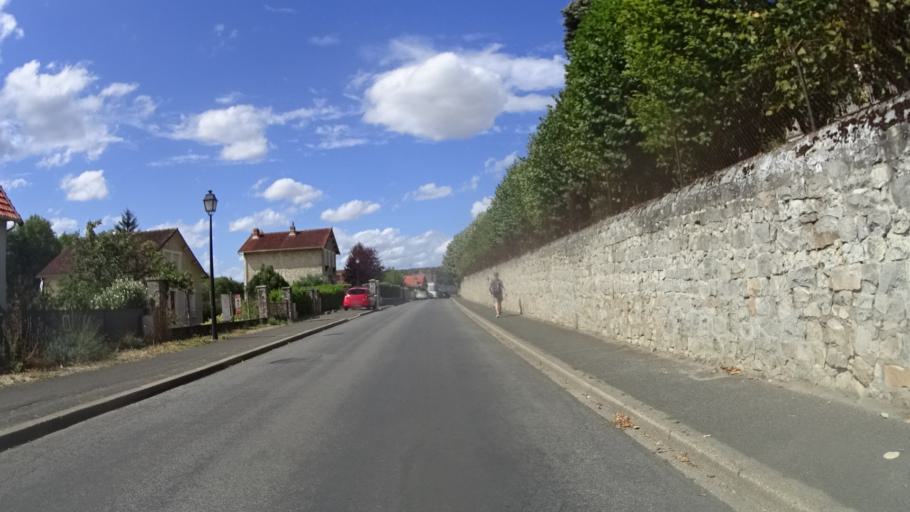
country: FR
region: Ile-de-France
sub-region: Departement de l'Essonne
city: Boutigny-sur-Essonne
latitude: 48.4321
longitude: 2.3800
